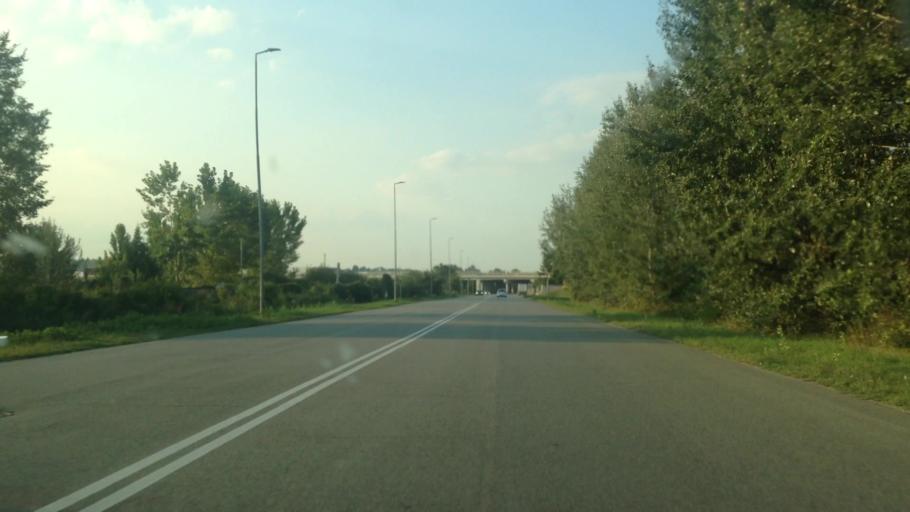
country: IT
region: Piedmont
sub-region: Provincia di Asti
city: Asti
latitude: 44.9092
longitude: 8.2305
